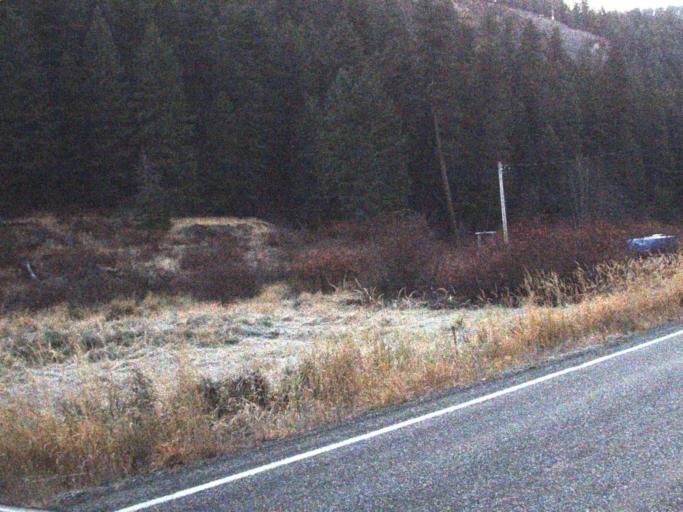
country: US
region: Washington
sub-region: Ferry County
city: Republic
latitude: 48.5336
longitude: -118.7367
